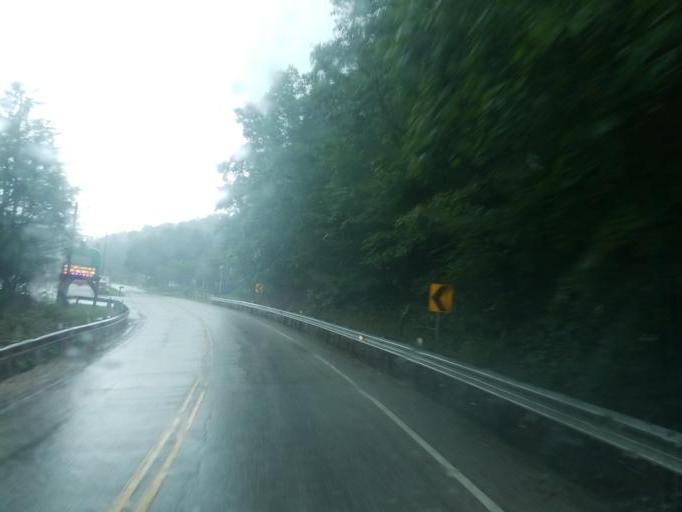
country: US
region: Kentucky
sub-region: Rowan County
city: Morehead
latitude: 38.2583
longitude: -83.3328
